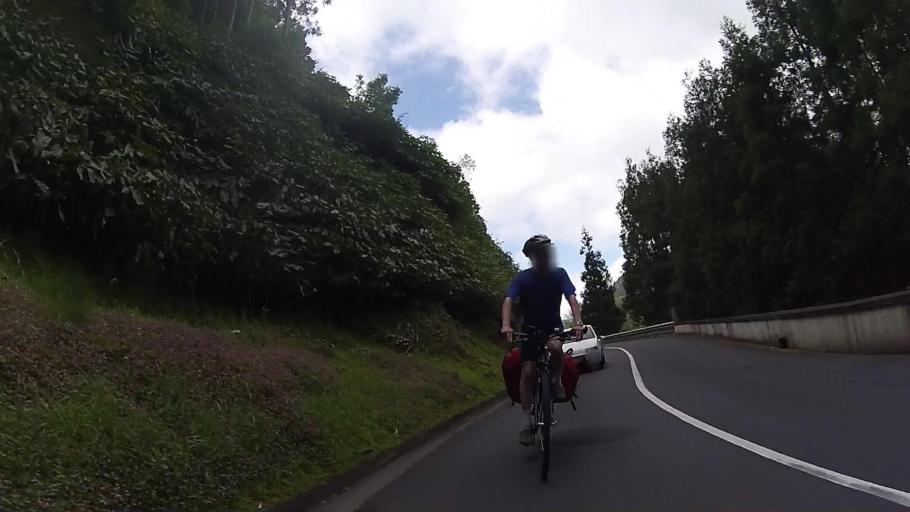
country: PT
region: Azores
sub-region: Povoacao
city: Furnas
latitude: 37.7667
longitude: -25.2882
